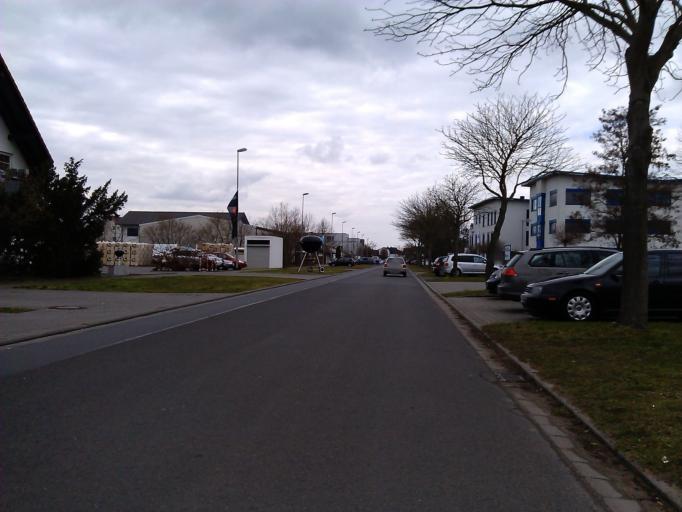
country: DE
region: Hesse
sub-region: Regierungsbezirk Darmstadt
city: Buttelborn
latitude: 49.8992
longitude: 8.5259
